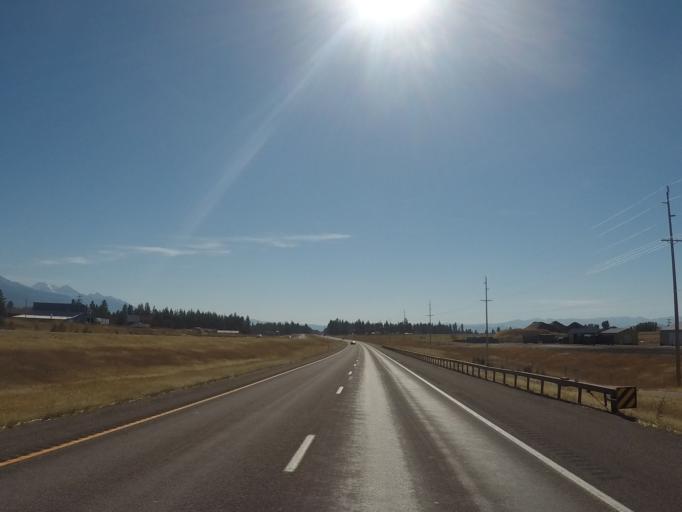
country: US
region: Montana
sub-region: Lake County
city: Pablo
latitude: 47.6382
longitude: -114.1142
